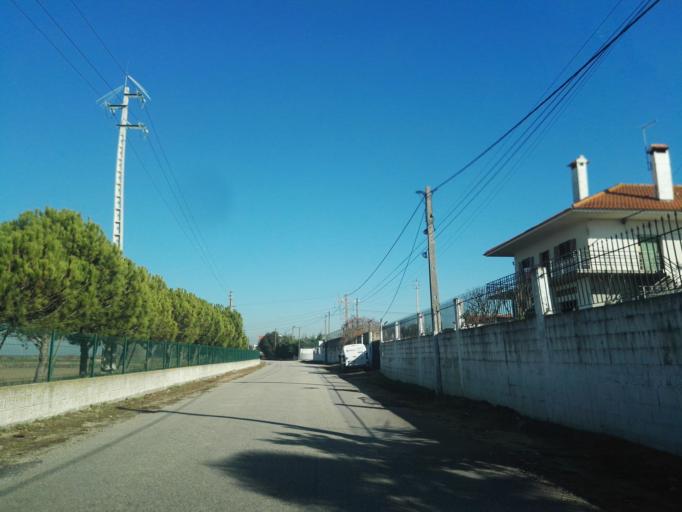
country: PT
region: Santarem
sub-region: Benavente
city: Samora Correia
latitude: 38.9294
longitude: -8.8847
